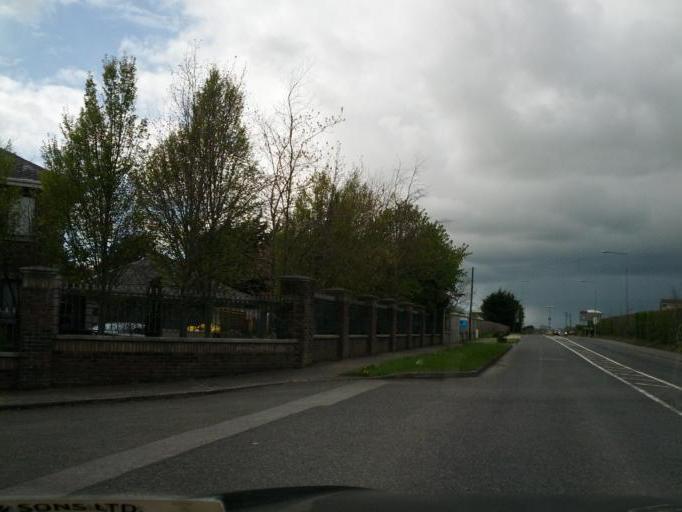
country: IE
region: Leinster
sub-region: An Mhi
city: Dunshaughlin
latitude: 53.5159
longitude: -6.5434
